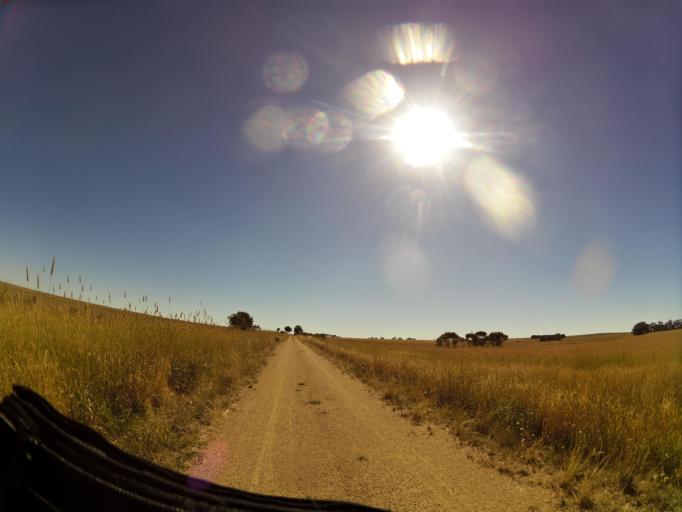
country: AU
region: Victoria
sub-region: Ballarat North
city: Delacombe
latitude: -37.6907
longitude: 143.3794
